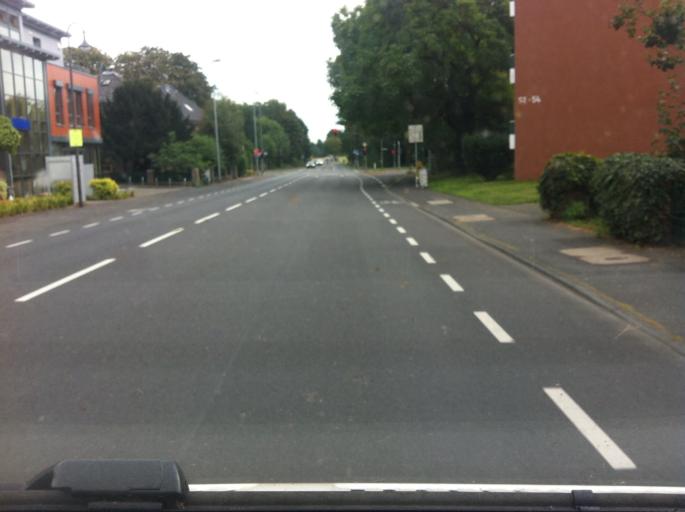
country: DE
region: North Rhine-Westphalia
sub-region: Regierungsbezirk Koln
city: Pulheim
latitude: 50.9580
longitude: 6.7892
